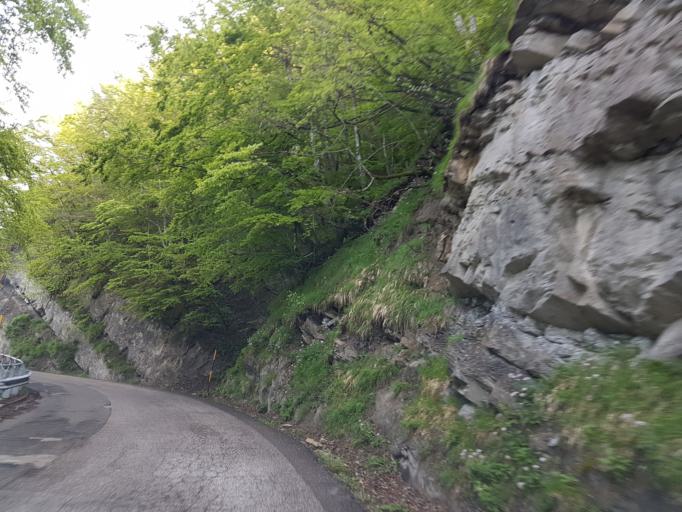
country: IT
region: Emilia-Romagna
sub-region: Forli-Cesena
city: San Piero in Bagno
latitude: 43.7996
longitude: 11.9137
